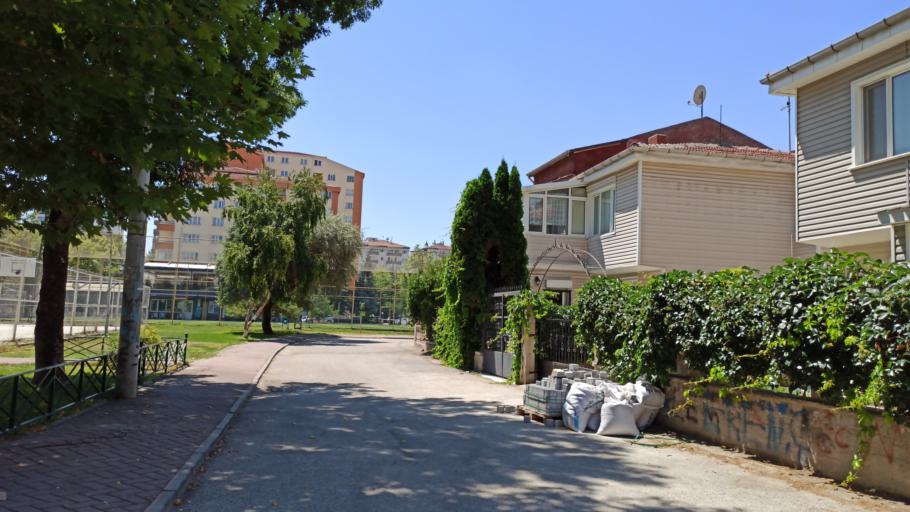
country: TR
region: Eskisehir
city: Eskisehir
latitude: 39.7665
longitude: 30.5042
